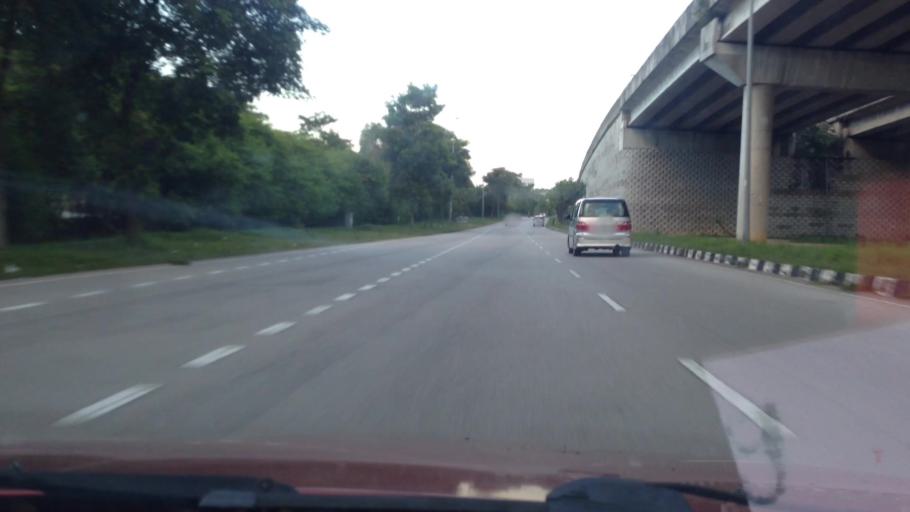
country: MY
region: Selangor
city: Shah Alam
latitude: 3.1004
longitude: 101.5478
